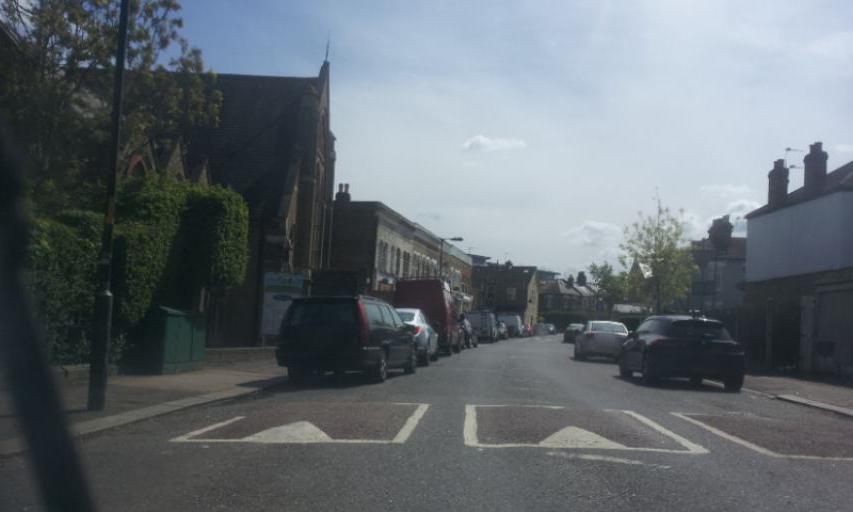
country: GB
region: England
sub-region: Greater London
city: Camberwell
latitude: 51.4571
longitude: -0.0674
